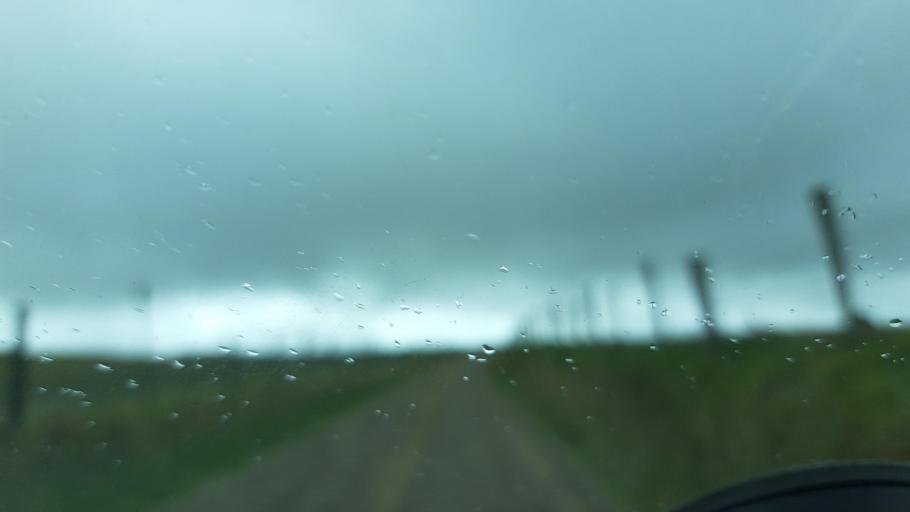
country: CO
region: Boyaca
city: Cucaita
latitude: 5.5119
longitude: -73.4414
